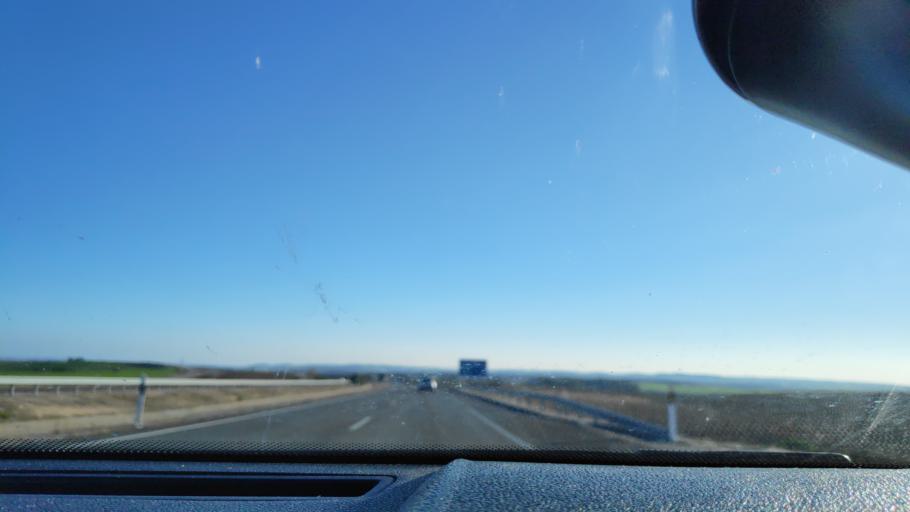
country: ES
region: Andalusia
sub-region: Provincia de Sevilla
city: Guillena
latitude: 37.5464
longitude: -6.1010
